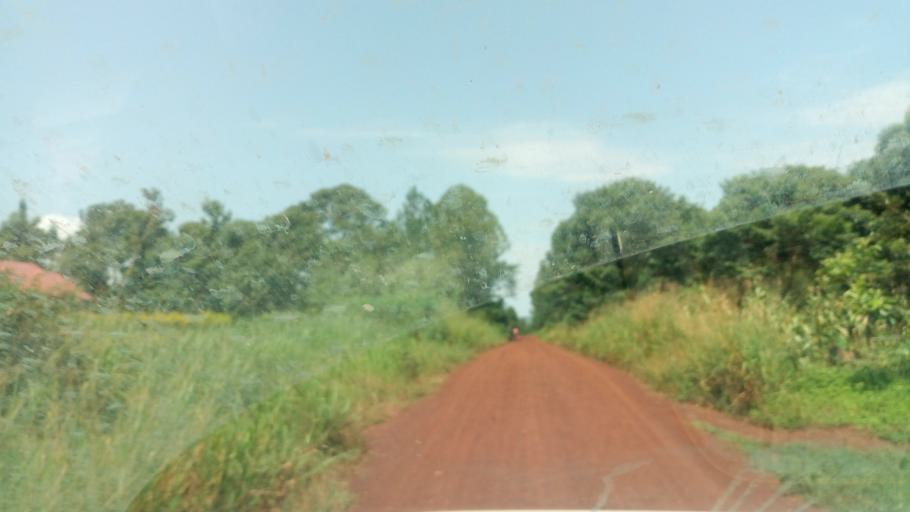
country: UG
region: Western Region
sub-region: Masindi District
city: Masindi
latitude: 1.6674
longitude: 31.8195
